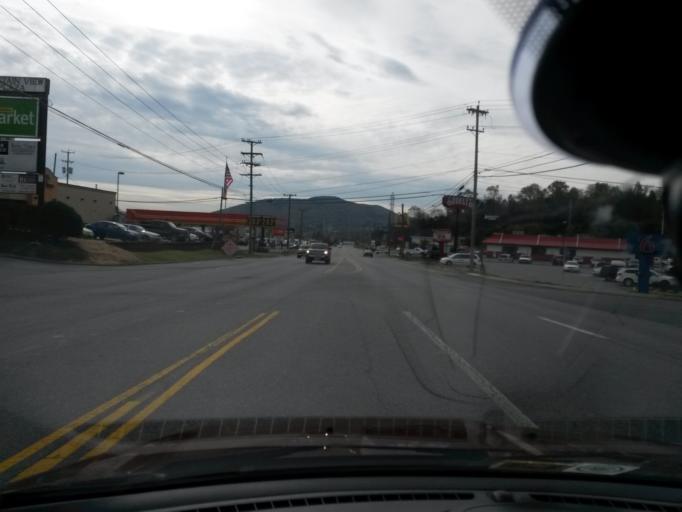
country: US
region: Virginia
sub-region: Botetourt County
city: Cloverdale
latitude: 37.3858
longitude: -79.9030
